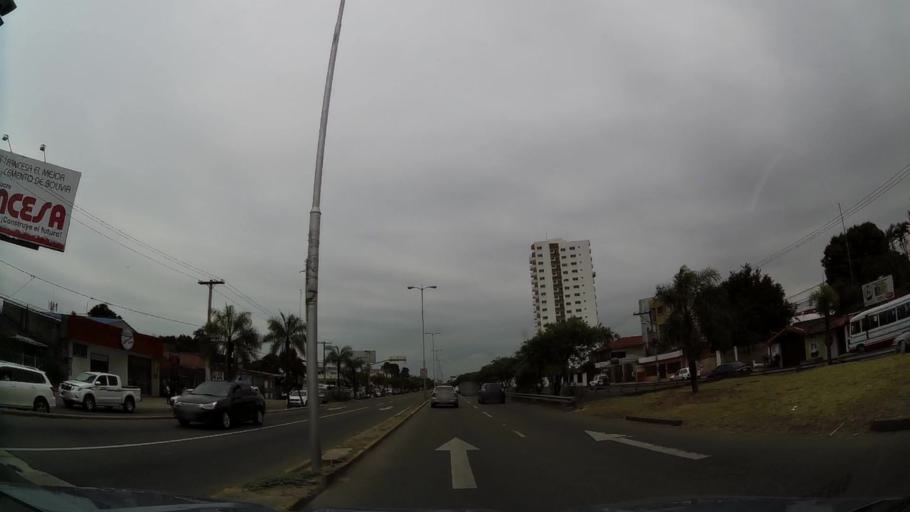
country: BO
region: Santa Cruz
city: Santa Cruz de la Sierra
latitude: -17.7797
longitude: -63.1937
